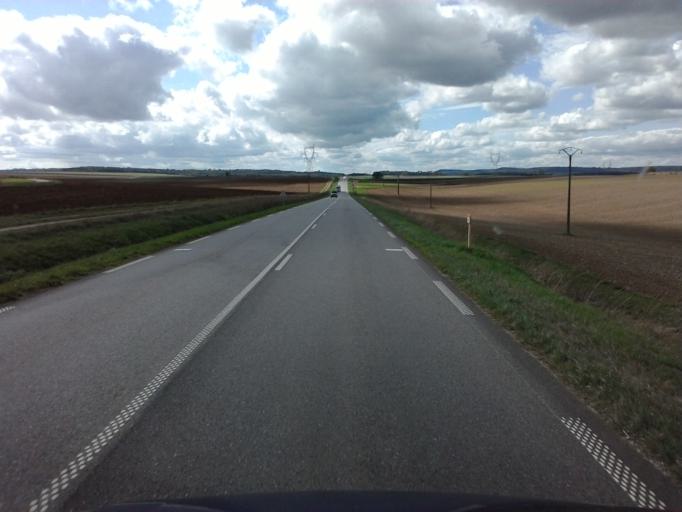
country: FR
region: Lorraine
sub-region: Departement de Meurthe-et-Moselle
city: Colombey-les-Belles
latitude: 48.4783
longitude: 5.8445
